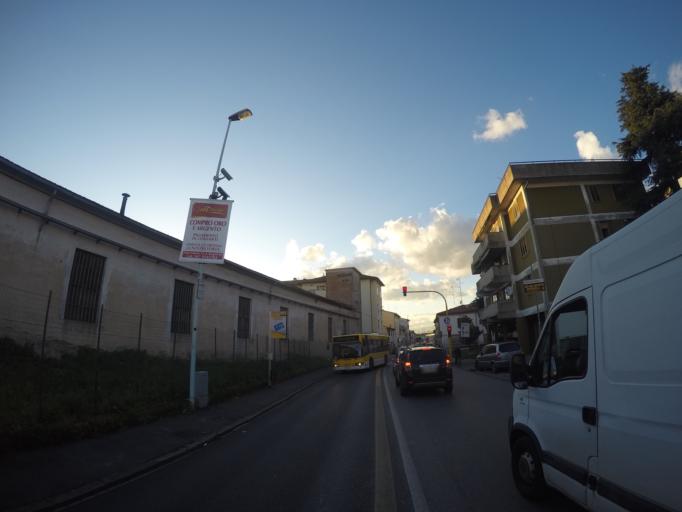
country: IT
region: Tuscany
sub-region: Provincia di Prato
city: Prato
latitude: 43.8902
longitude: 11.0779
